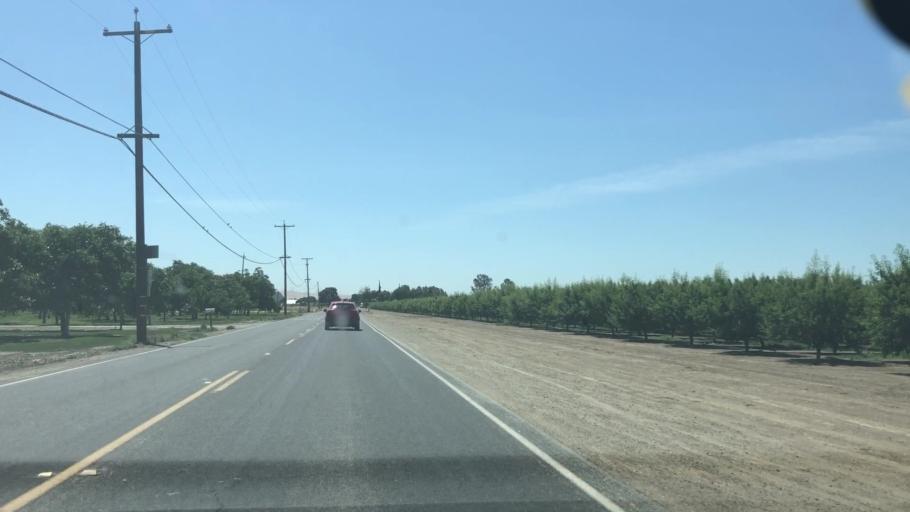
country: US
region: California
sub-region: San Joaquin County
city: Tracy
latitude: 37.7252
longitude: -121.3993
